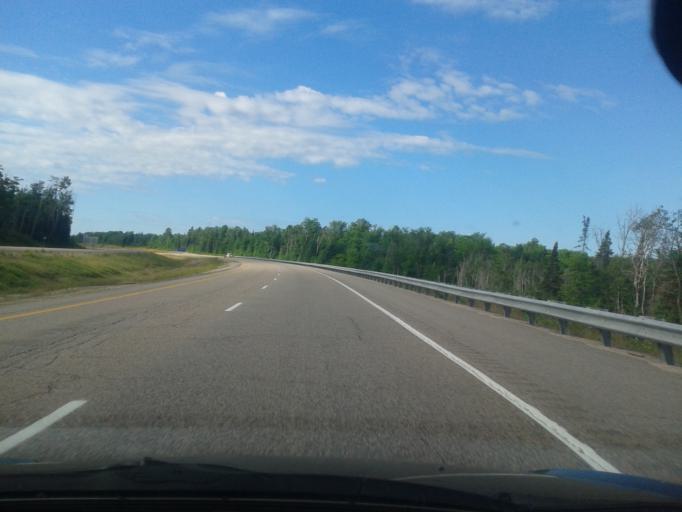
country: CA
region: Ontario
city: South River
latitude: 45.8908
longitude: -79.3794
